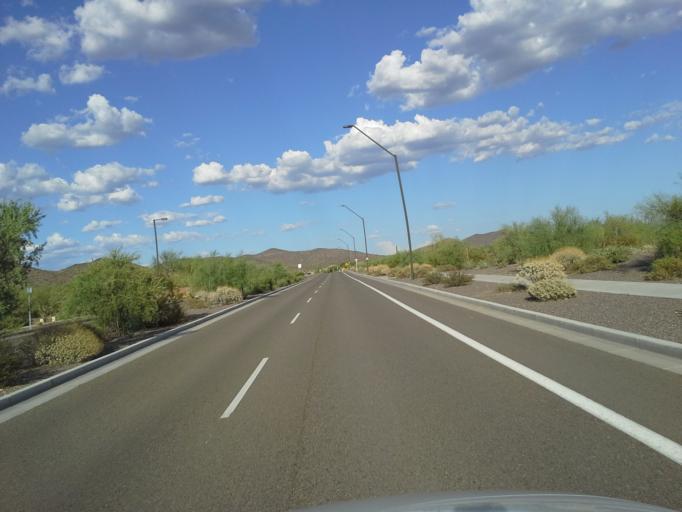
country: US
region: Arizona
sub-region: Maricopa County
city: Anthem
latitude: 33.7838
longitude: -112.1055
